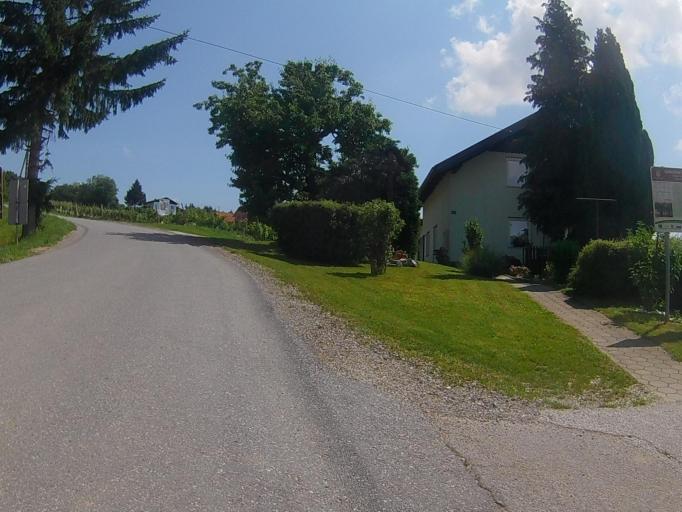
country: SI
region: Pesnica
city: Pesnica pri Mariboru
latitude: 46.5717
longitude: 15.6957
